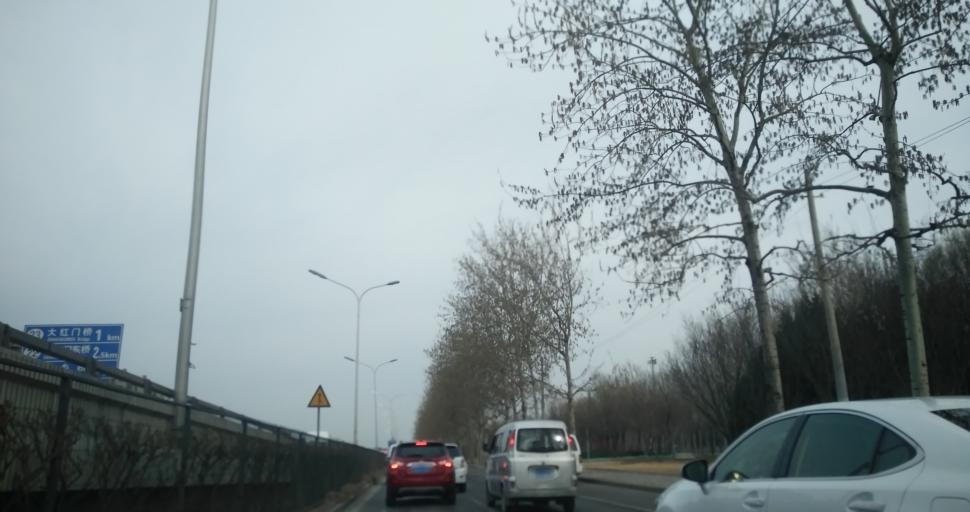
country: CN
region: Beijing
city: Dahongmen
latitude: 39.8300
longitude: 116.3754
